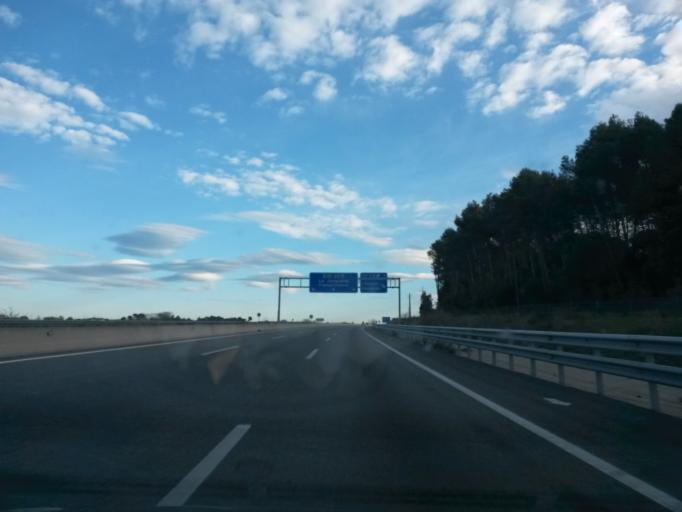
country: ES
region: Catalonia
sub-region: Provincia de Girona
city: Vilademuls
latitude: 42.1210
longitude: 2.9121
